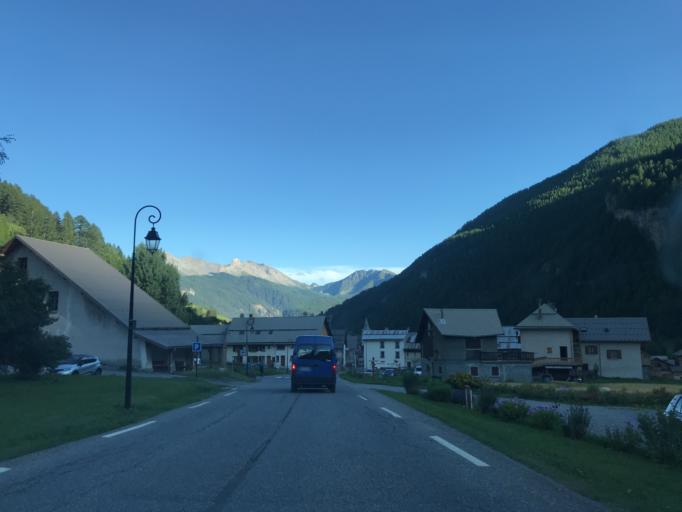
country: FR
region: Provence-Alpes-Cote d'Azur
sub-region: Departement des Hautes-Alpes
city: Guillestre
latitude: 44.7691
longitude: 6.7372
